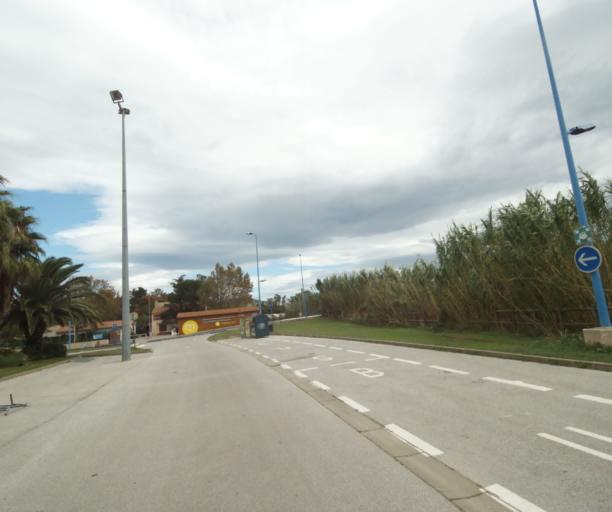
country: FR
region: Languedoc-Roussillon
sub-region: Departement des Pyrenees-Orientales
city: Argelers
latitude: 42.5501
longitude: 3.0304
